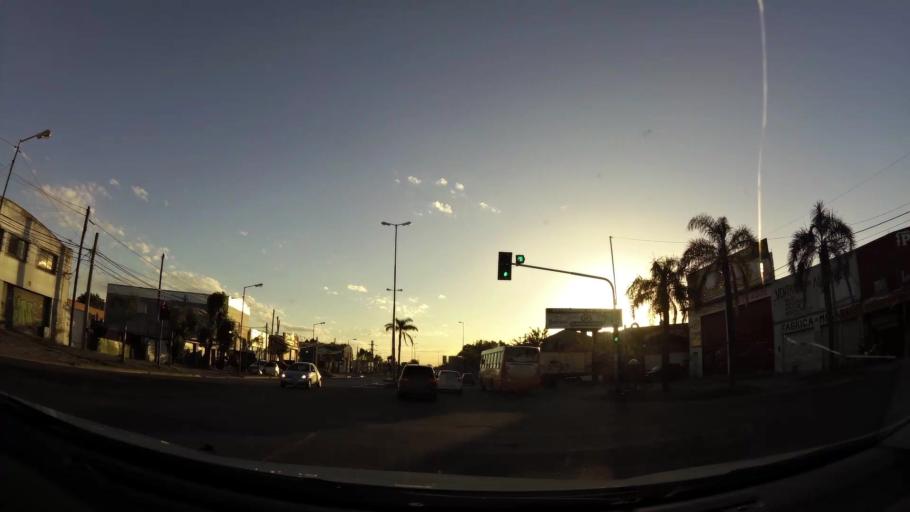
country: AR
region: Buenos Aires
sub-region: Partido de Tigre
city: Tigre
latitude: -34.4411
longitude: -58.5756
